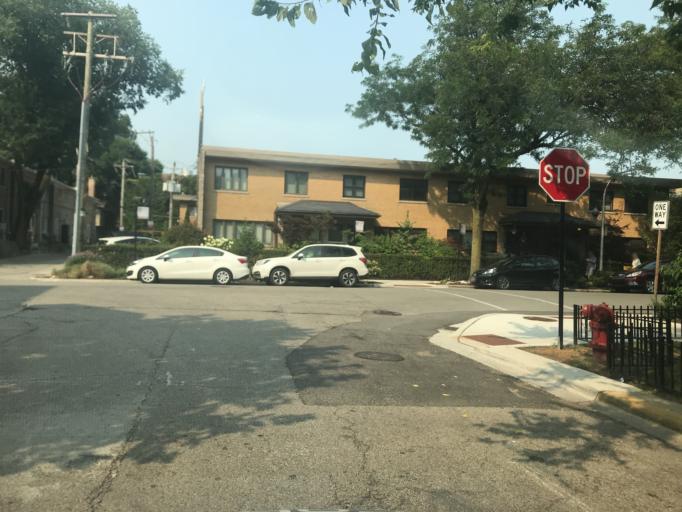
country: US
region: Illinois
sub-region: Cook County
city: Chicago
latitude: 41.9471
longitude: -87.6447
